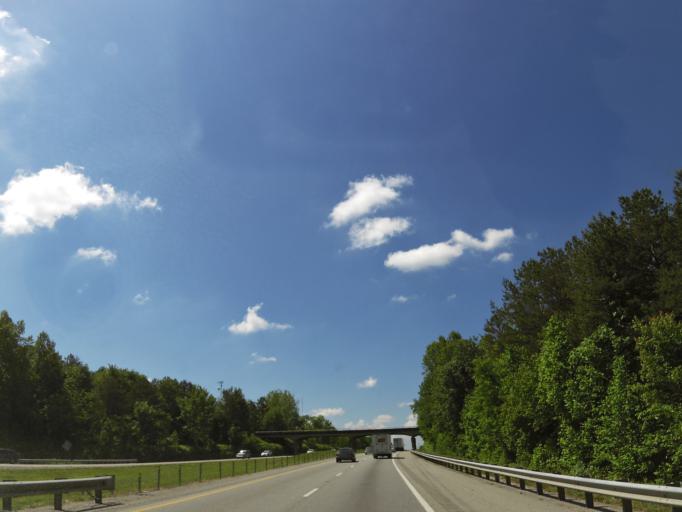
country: US
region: Kentucky
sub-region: Laurel County
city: North Corbin
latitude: 37.0204
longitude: -84.1000
